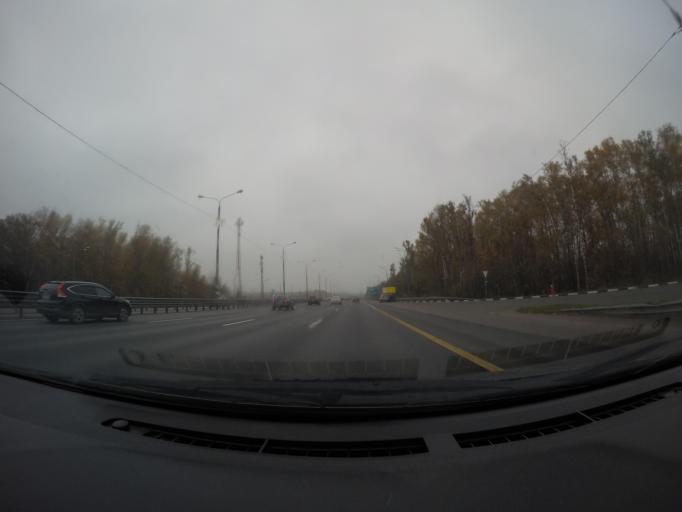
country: RU
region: Moskovskaya
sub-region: Podol'skiy Rayon
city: Podol'sk
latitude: 55.3948
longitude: 37.6052
